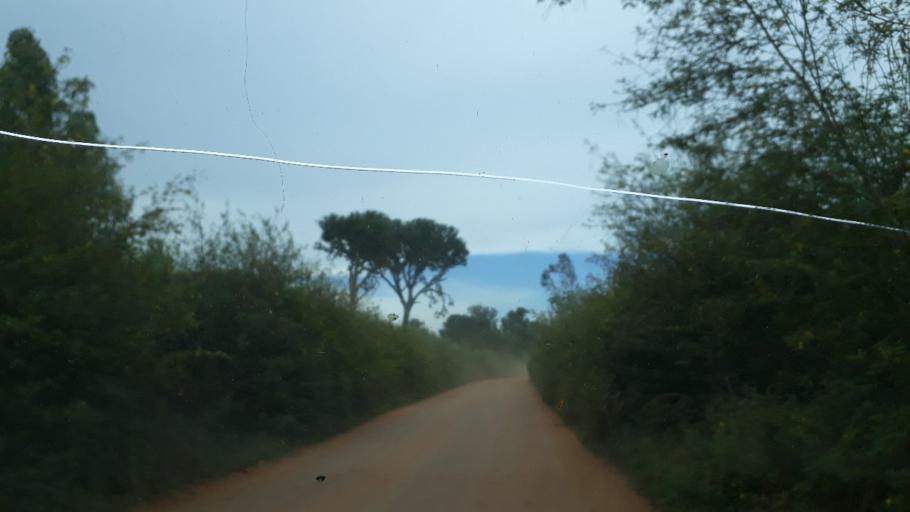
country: CD
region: Eastern Province
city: Bunia
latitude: 1.8986
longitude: 30.4977
